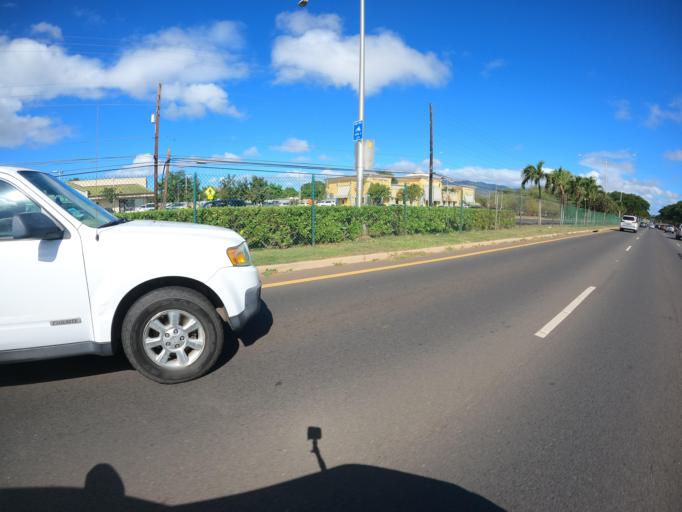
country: US
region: Hawaii
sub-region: Honolulu County
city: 'Ewa Gentry
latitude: 21.3503
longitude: -158.0267
